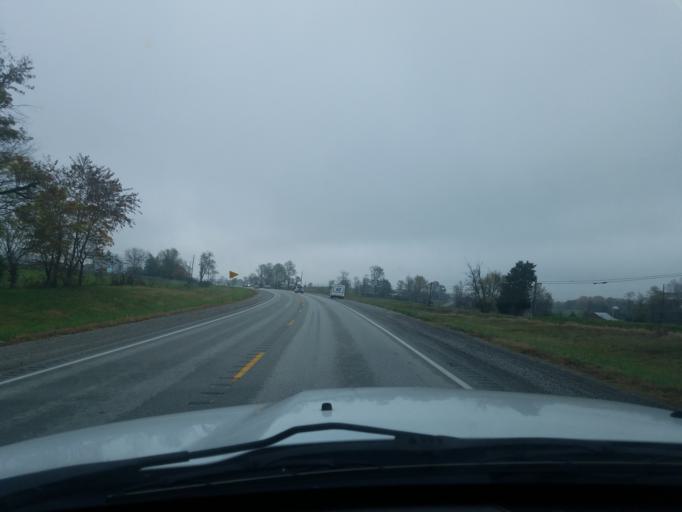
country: US
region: Kentucky
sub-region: Taylor County
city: Campbellsville
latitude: 37.3781
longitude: -85.2981
